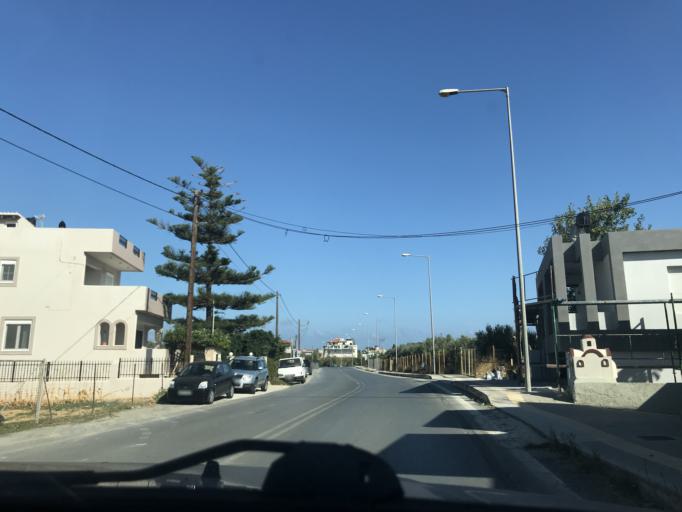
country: GR
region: Crete
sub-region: Nomos Irakleiou
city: Gazi
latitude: 35.3289
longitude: 25.0641
